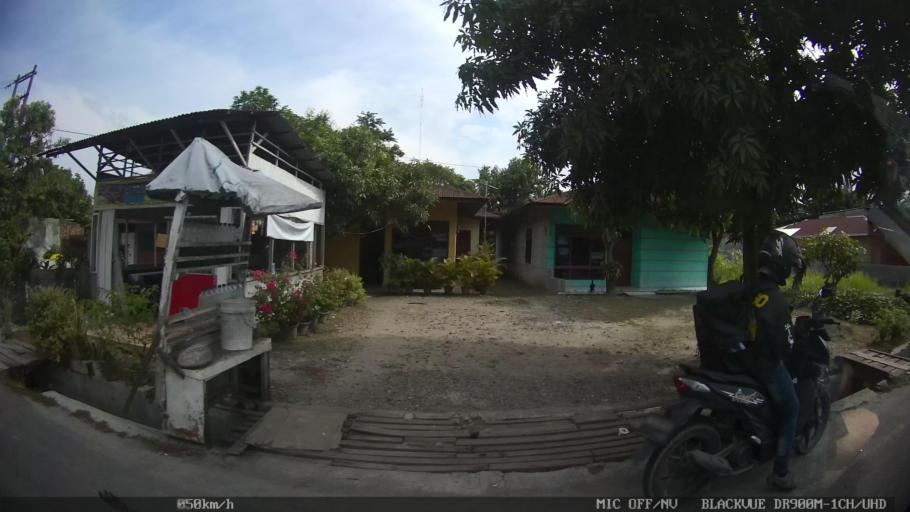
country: ID
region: North Sumatra
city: Percut
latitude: 3.6071
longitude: 98.7726
